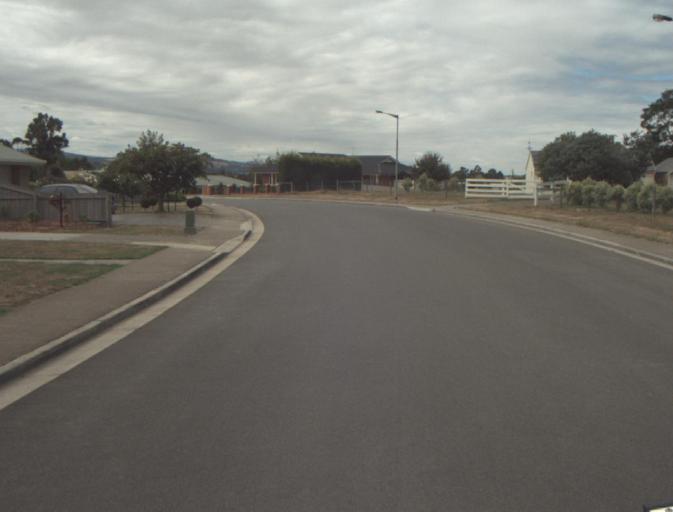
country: AU
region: Tasmania
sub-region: Launceston
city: Invermay
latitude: -41.3931
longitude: 147.1173
